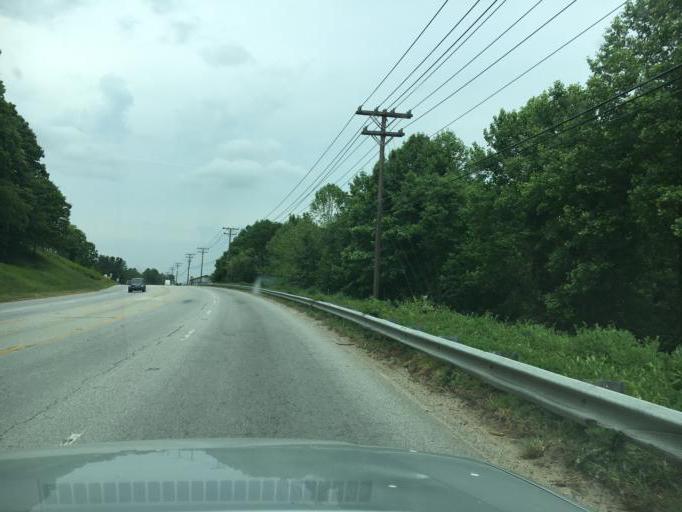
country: US
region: North Carolina
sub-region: Henderson County
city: Balfour
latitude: 35.3581
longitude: -82.4771
